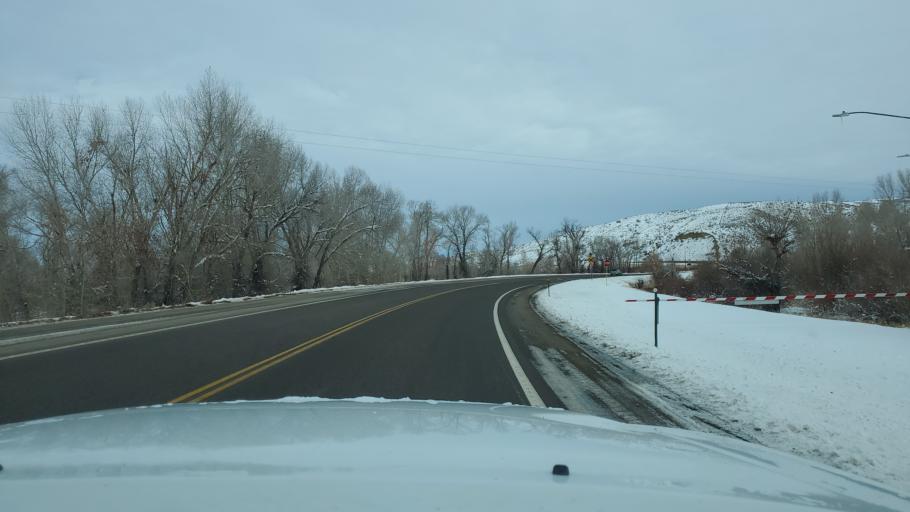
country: US
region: Colorado
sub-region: Routt County
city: Hayden
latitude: 40.5015
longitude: -107.3776
